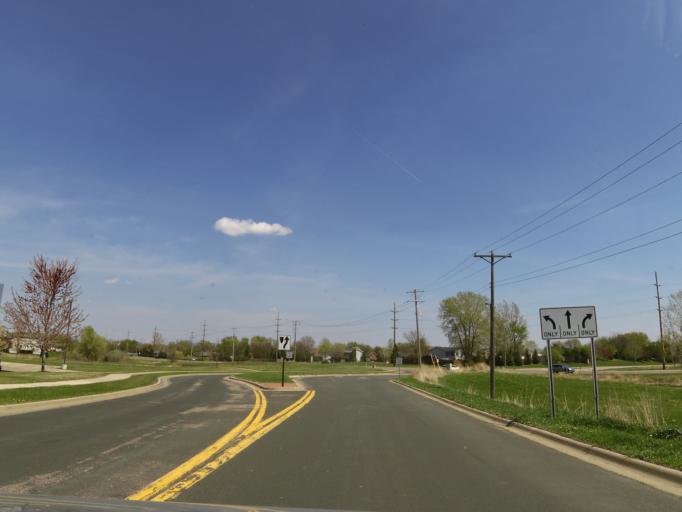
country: US
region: Minnesota
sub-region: Scott County
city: Savage
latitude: 44.7495
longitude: -93.3605
